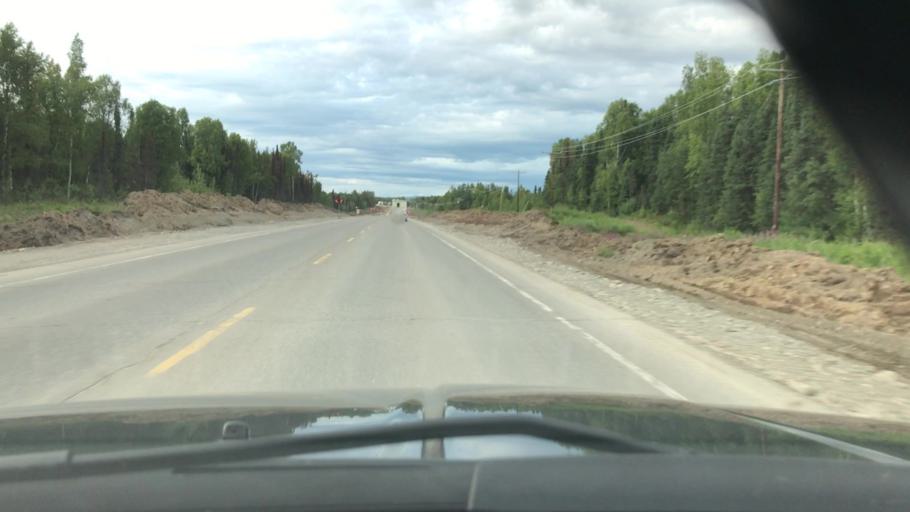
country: US
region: Alaska
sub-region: Matanuska-Susitna Borough
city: Y
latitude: 62.1180
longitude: -150.0487
